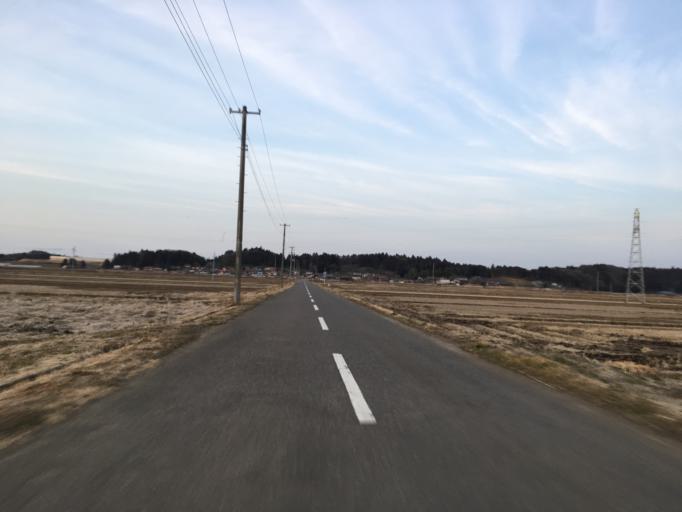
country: JP
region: Fukushima
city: Ishikawa
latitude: 37.0571
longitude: 140.3475
